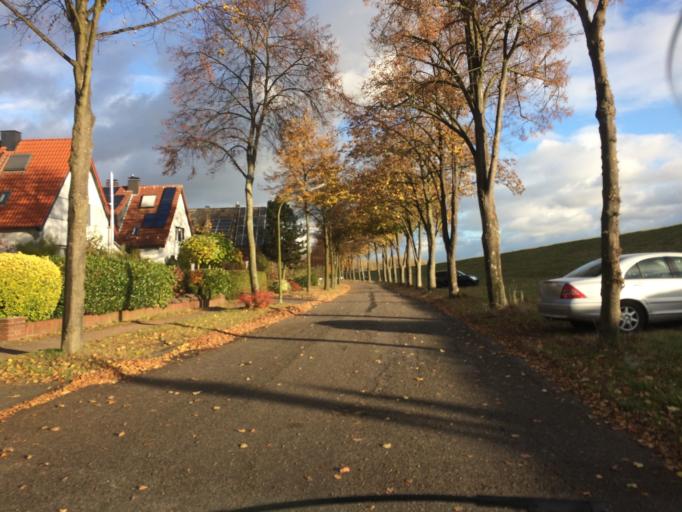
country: DE
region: North Rhine-Westphalia
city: Dorsten
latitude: 51.6664
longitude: 6.9767
